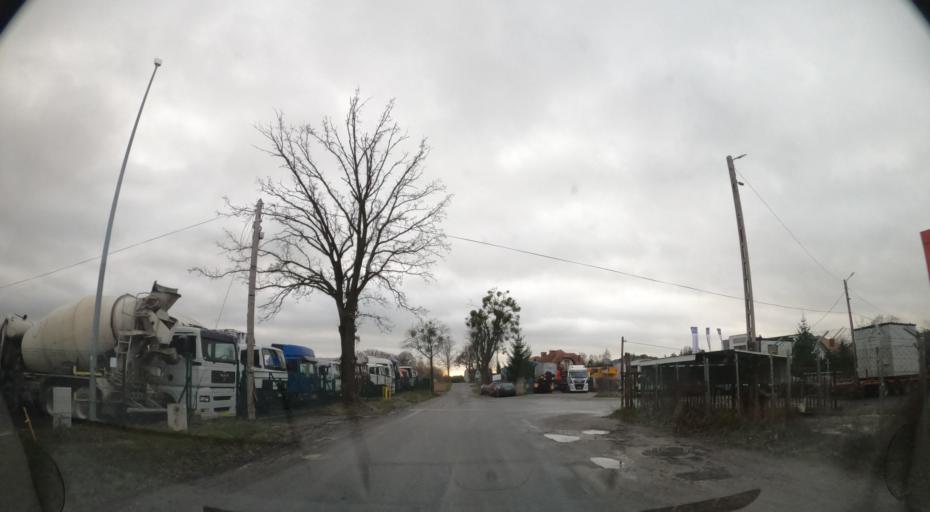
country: PL
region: Kujawsko-Pomorskie
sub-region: Powiat bydgoski
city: Sicienko
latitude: 53.1575
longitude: 17.8488
